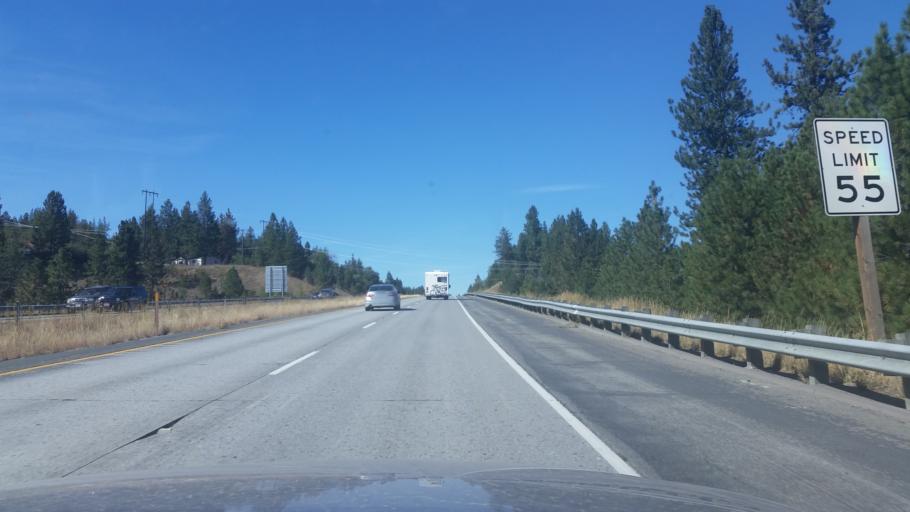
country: US
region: Washington
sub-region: Spokane County
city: Spokane
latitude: 47.6260
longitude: -117.4405
